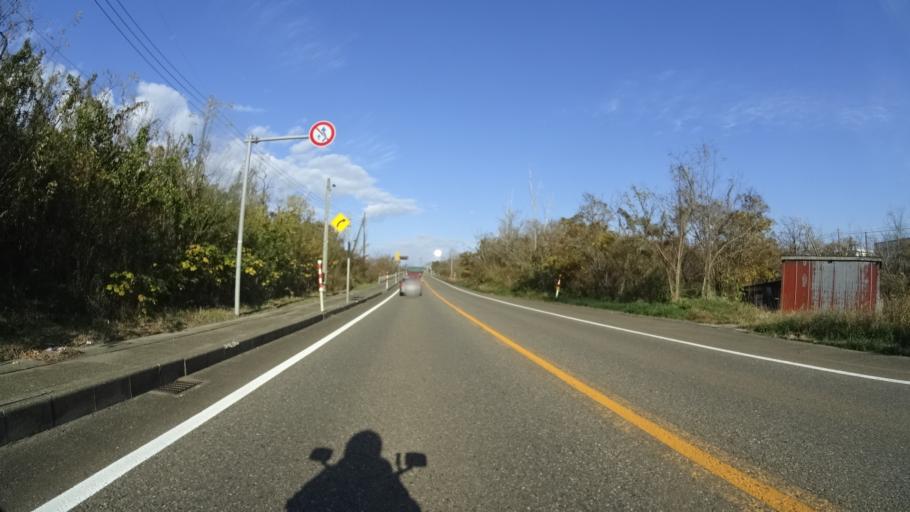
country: JP
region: Niigata
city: Joetsu
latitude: 37.2616
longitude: 138.3716
